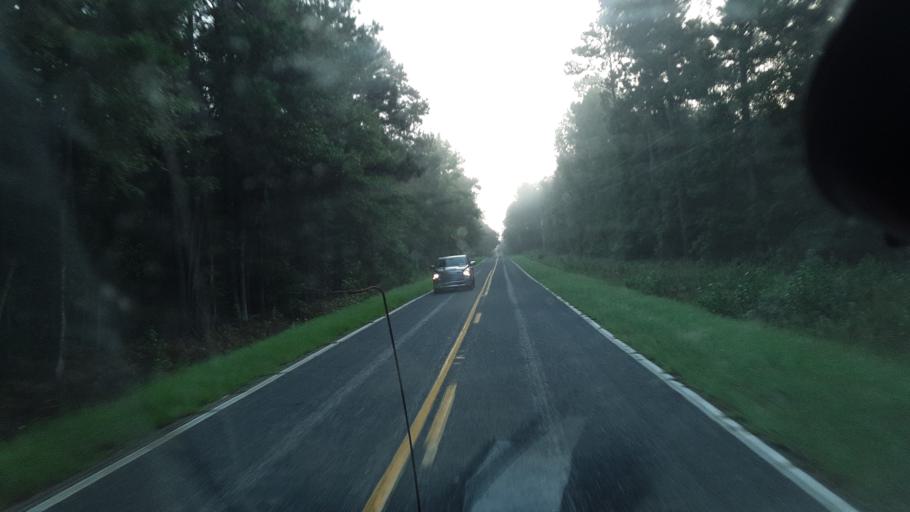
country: US
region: South Carolina
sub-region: Clarendon County
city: Manning
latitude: 33.7482
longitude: -80.0728
